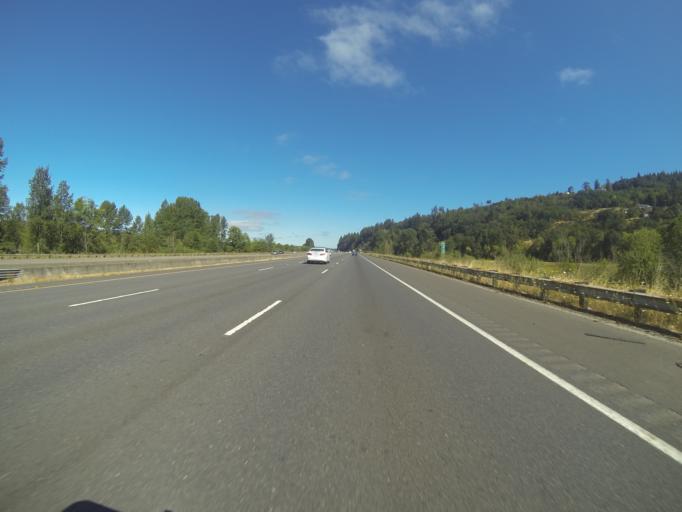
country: US
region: Washington
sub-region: Cowlitz County
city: Kalama
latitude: 46.0511
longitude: -122.8621
